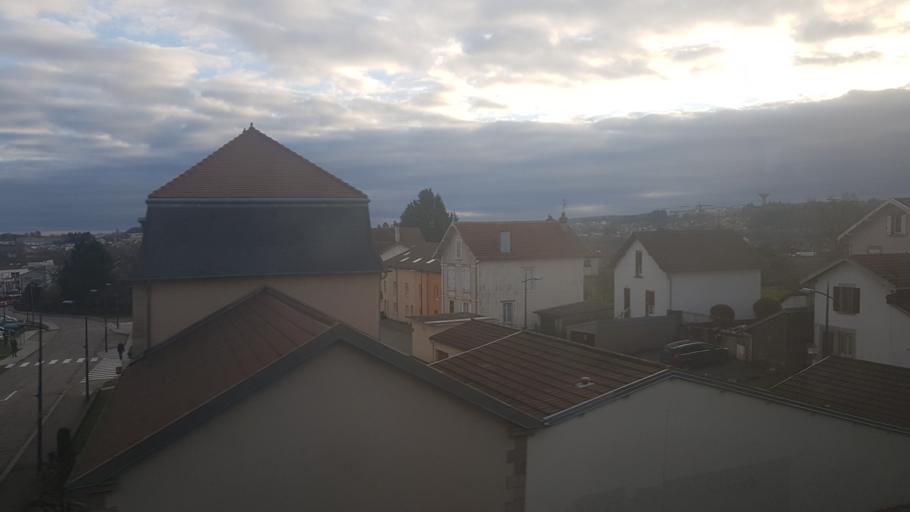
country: FR
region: Lorraine
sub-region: Departement des Vosges
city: Golbey
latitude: 48.1968
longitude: 6.4352
